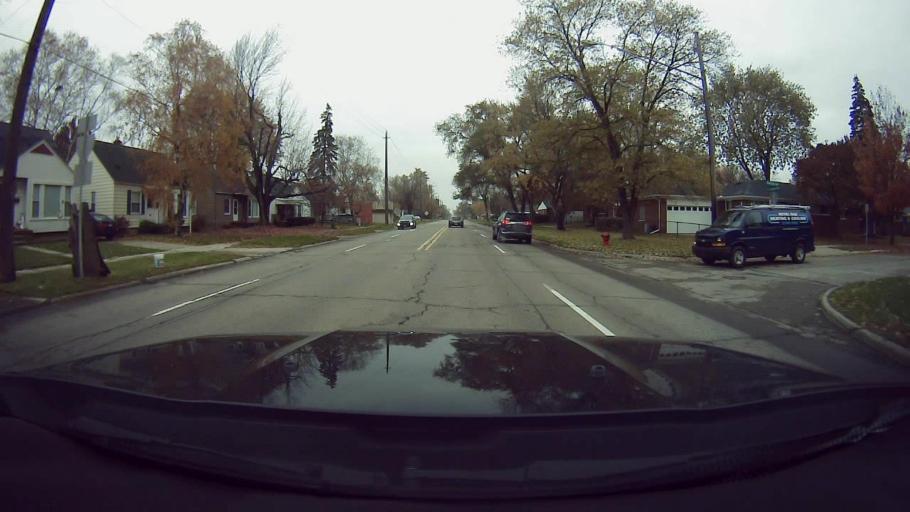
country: US
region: Michigan
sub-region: Oakland County
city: Pleasant Ridge
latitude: 42.4777
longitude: -83.1238
